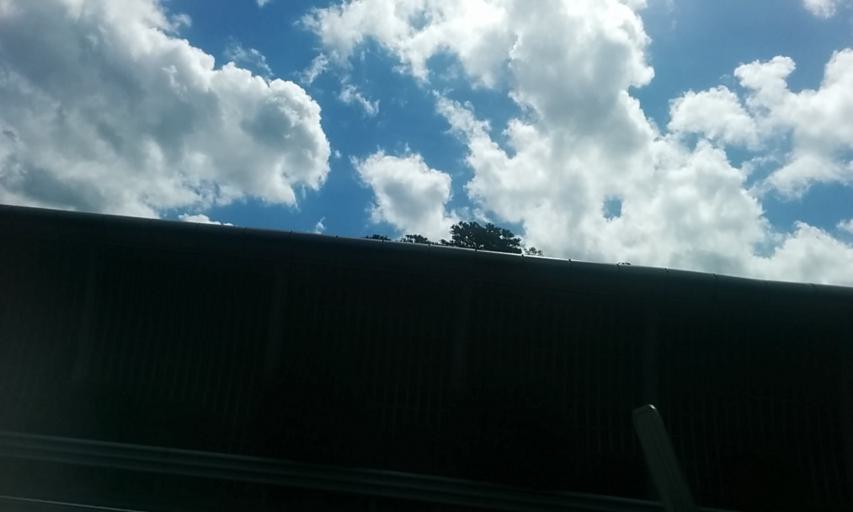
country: JP
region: Shiga Prefecture
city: Otsu-shi
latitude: 34.9524
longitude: 135.9022
